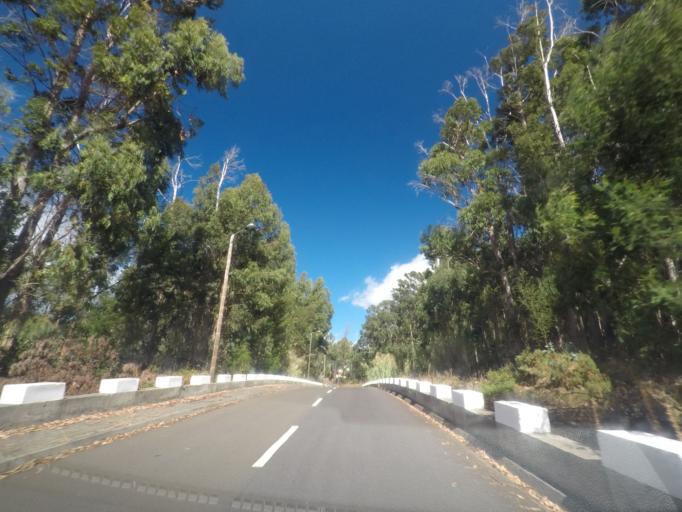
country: PT
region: Madeira
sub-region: Ribeira Brava
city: Campanario
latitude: 32.6875
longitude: -17.0395
